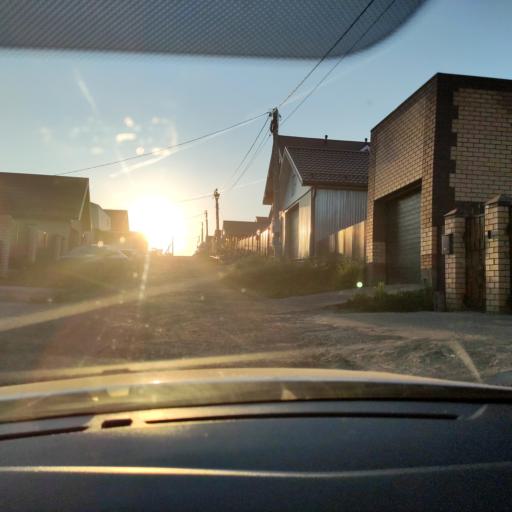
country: RU
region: Tatarstan
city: Stolbishchi
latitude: 55.7514
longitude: 49.3041
